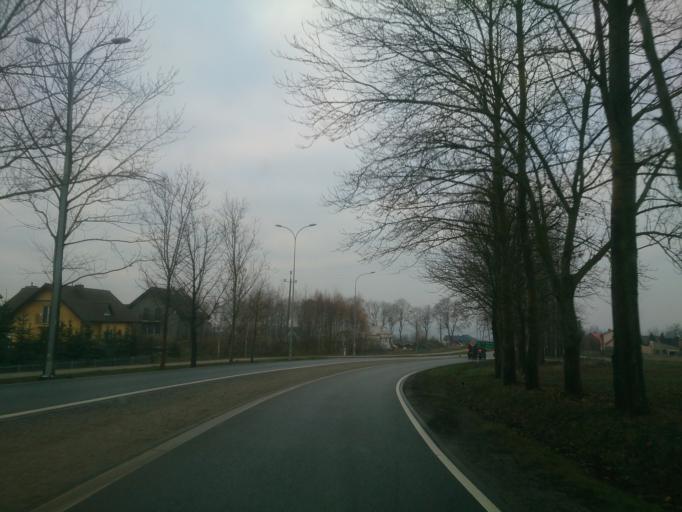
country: PL
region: Pomeranian Voivodeship
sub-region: Powiat bytowski
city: Bytow
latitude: 54.1618
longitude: 17.5177
